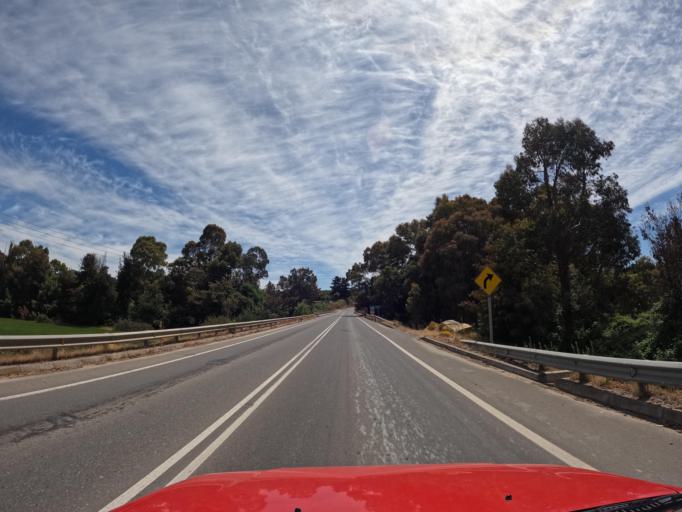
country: CL
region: Maule
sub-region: Provincia de Talca
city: Talca
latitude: -35.2792
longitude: -71.5353
